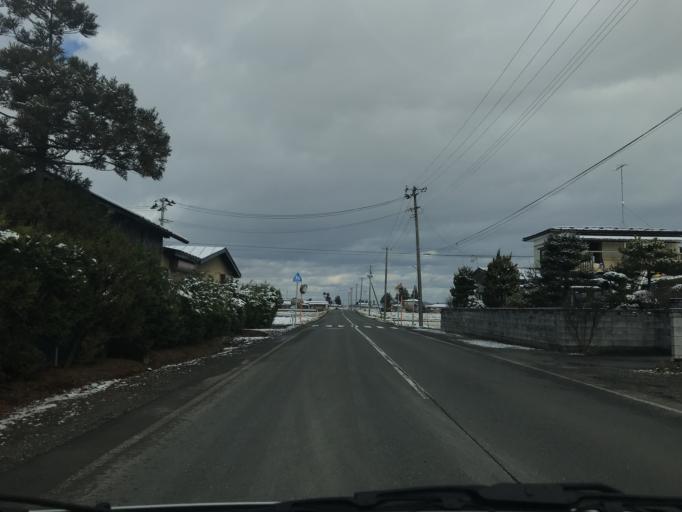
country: JP
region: Iwate
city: Mizusawa
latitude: 39.1510
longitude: 141.1134
